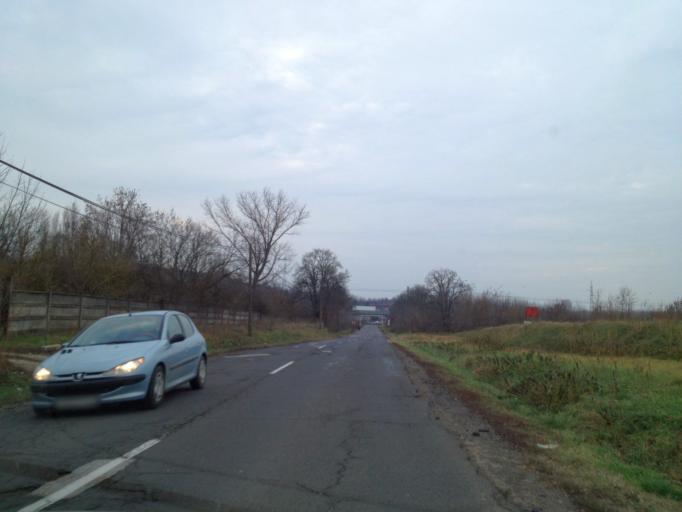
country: HU
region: Heves
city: Hatvan
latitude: 47.6918
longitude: 19.6925
